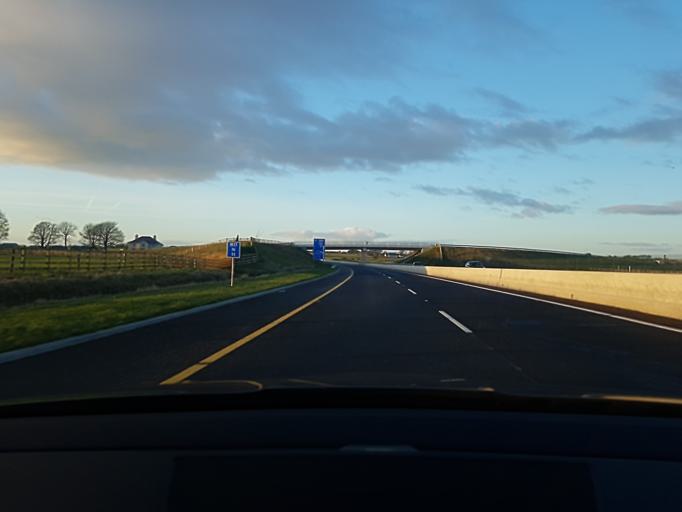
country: IE
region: Connaught
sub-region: County Galway
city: Athenry
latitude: 53.3913
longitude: -8.8027
